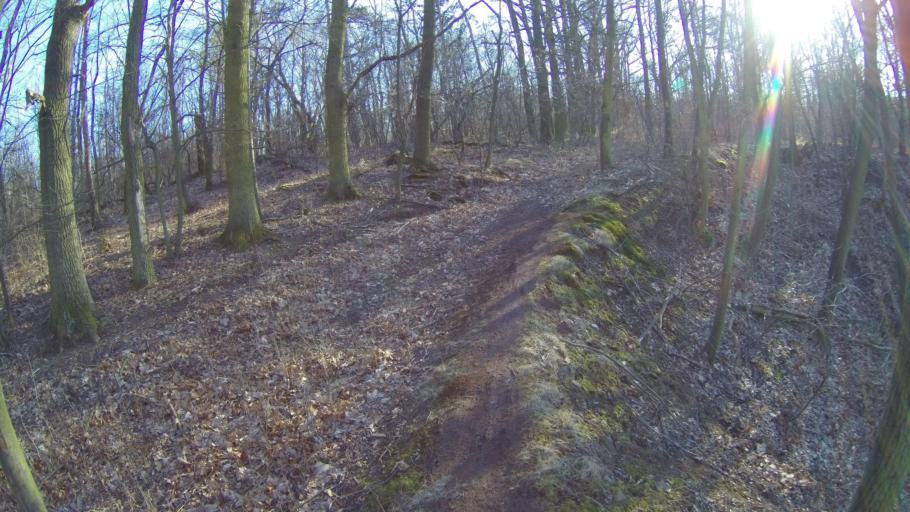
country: CZ
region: Central Bohemia
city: Neratovice
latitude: 50.2328
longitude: 14.5068
